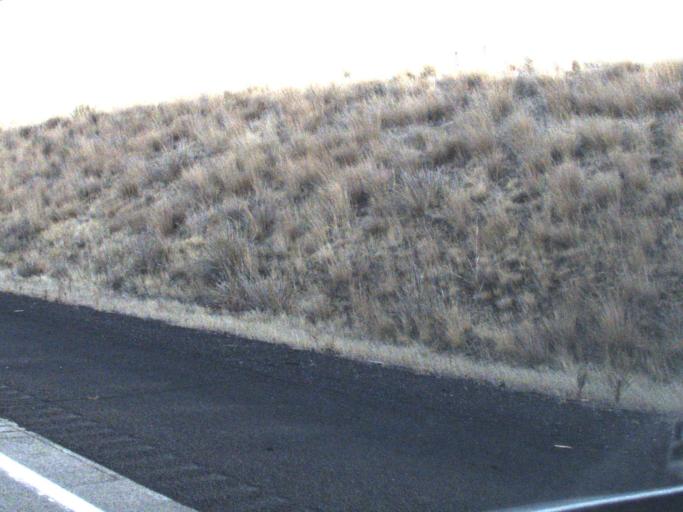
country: US
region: Washington
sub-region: Adams County
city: Ritzville
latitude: 46.9083
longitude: -118.6094
